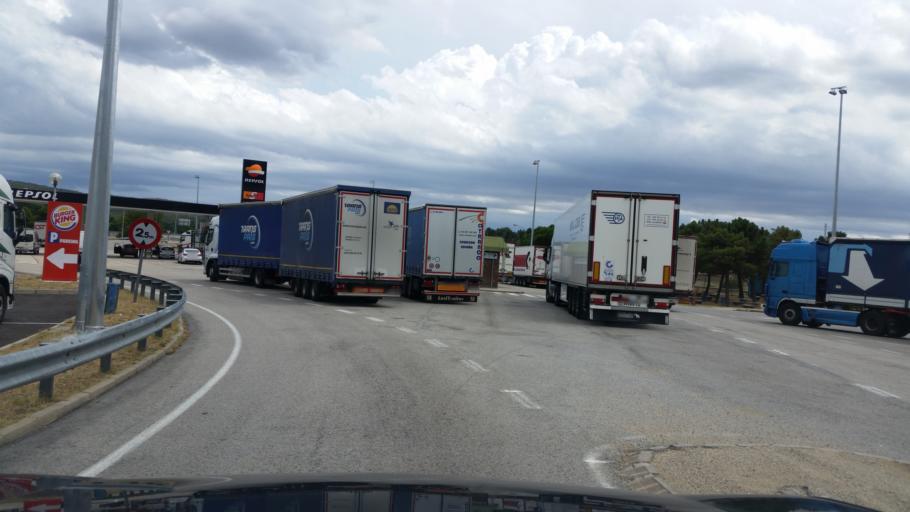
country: ES
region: Catalonia
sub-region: Provincia de Girona
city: la Jonquera
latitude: 42.4058
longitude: 2.8715
